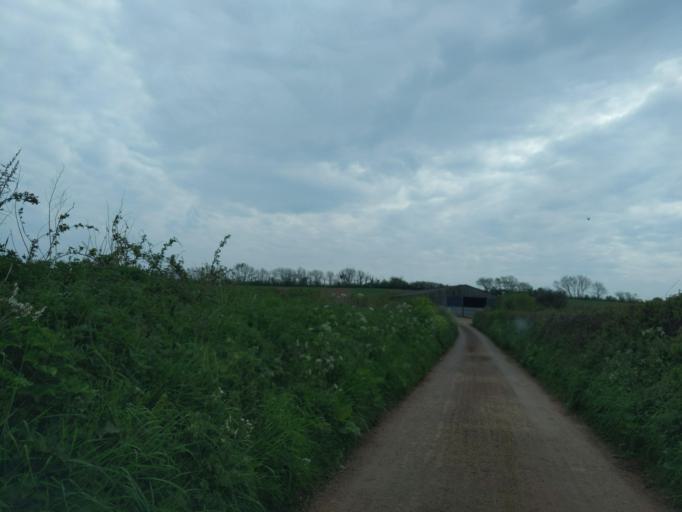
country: GB
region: England
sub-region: Devon
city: Yealmpton
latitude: 50.3637
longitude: -4.0242
